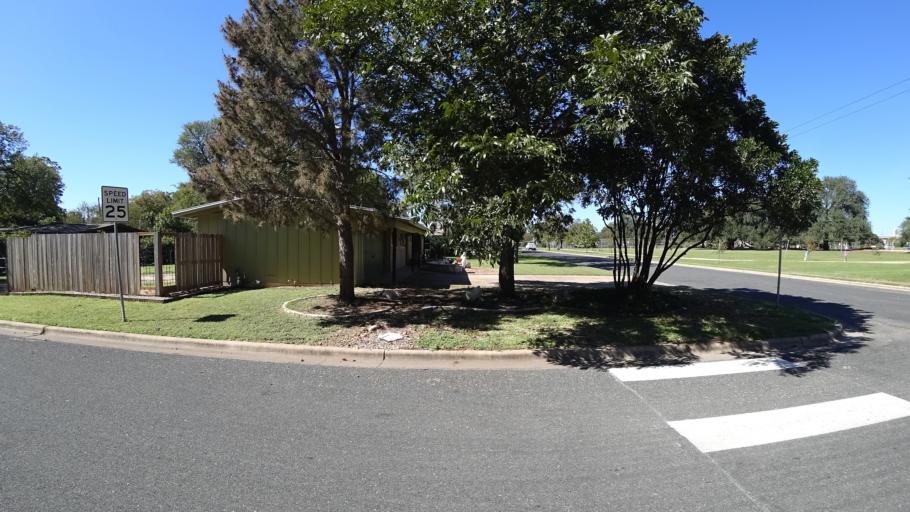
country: US
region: Texas
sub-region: Travis County
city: Rollingwood
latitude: 30.2276
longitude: -97.7917
